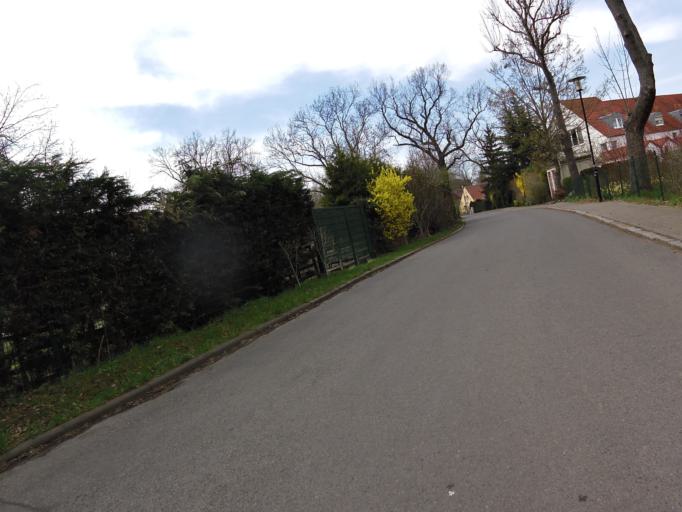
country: DE
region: Saxony
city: Schkeuditz
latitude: 51.3819
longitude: 12.2747
